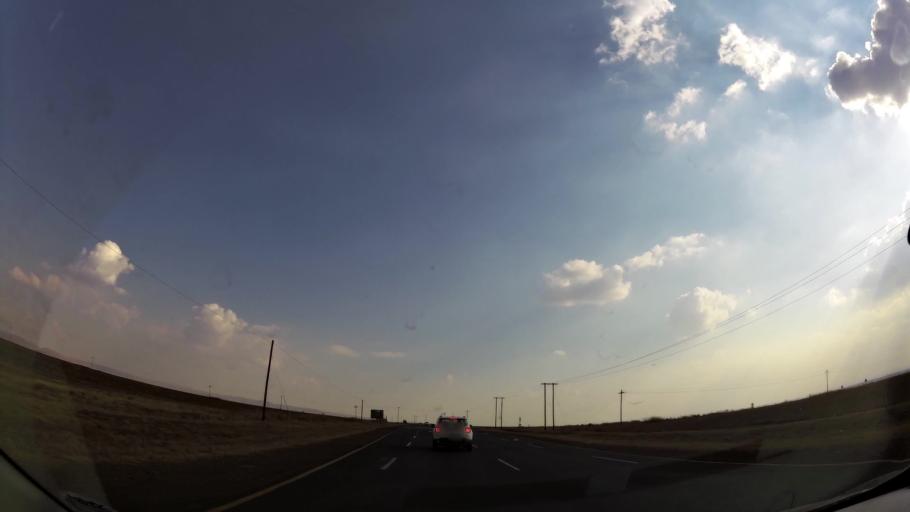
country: ZA
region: Gauteng
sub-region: Sedibeng District Municipality
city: Heidelberg
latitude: -26.3884
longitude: 28.2979
